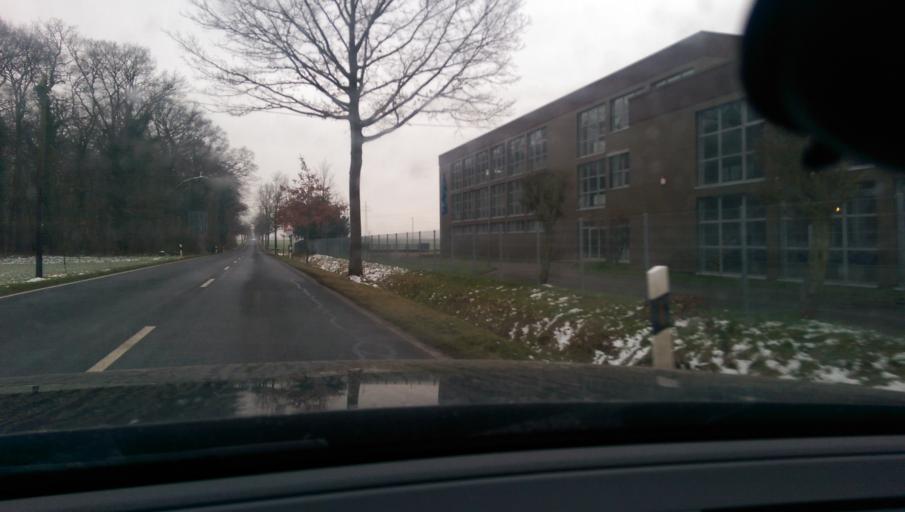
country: DE
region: Lower Saxony
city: Gross Munzel
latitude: 52.3884
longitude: 9.5128
